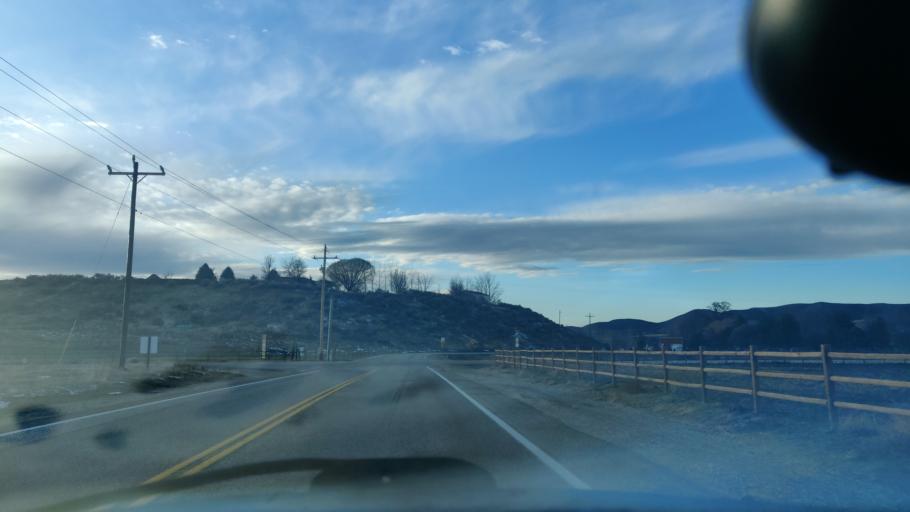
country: US
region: Idaho
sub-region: Ada County
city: Eagle
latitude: 43.7300
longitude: -116.2678
